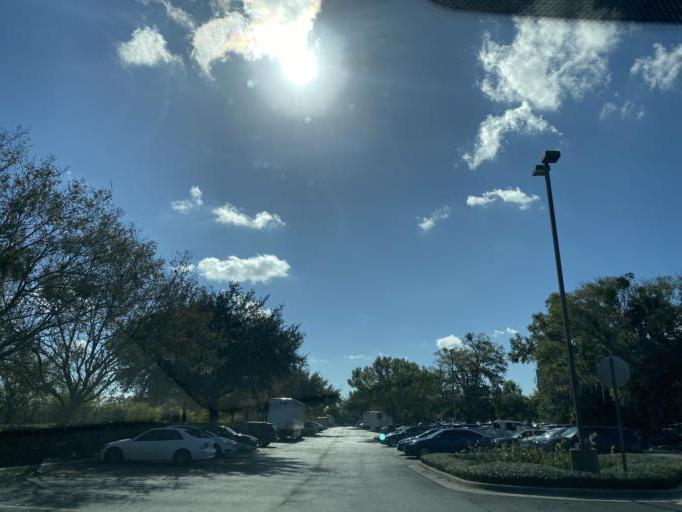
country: US
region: Florida
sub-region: Seminole County
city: Heathrow
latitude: 28.7903
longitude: -81.3519
